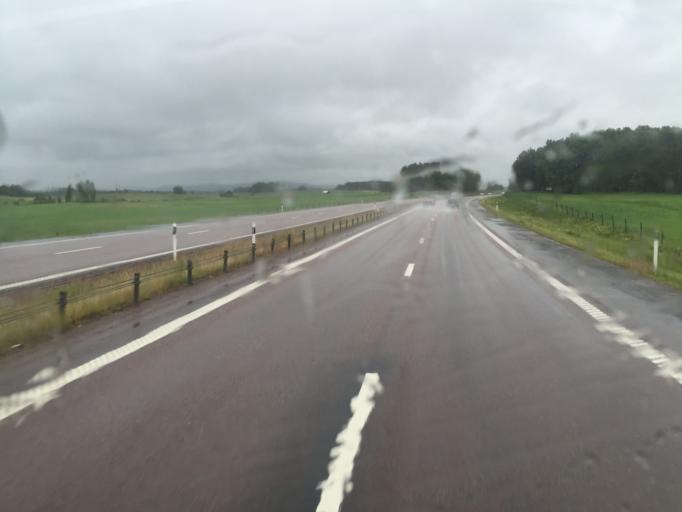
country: SE
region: Dalarna
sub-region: Borlange Kommun
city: Ornas
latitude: 60.4987
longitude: 15.5129
